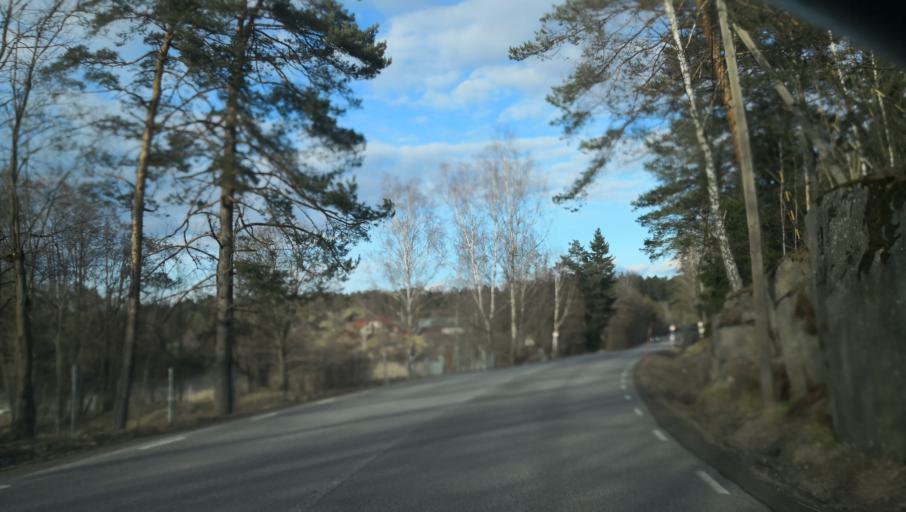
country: SE
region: Stockholm
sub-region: Varmdo Kommun
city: Gustavsberg
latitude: 59.3476
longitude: 18.3626
